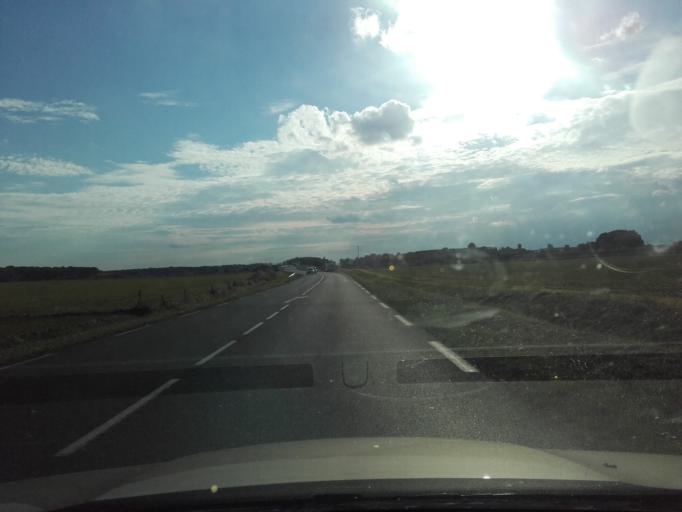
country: FR
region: Centre
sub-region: Departement d'Indre-et-Loire
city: Monnaie
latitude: 47.4779
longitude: 0.7610
